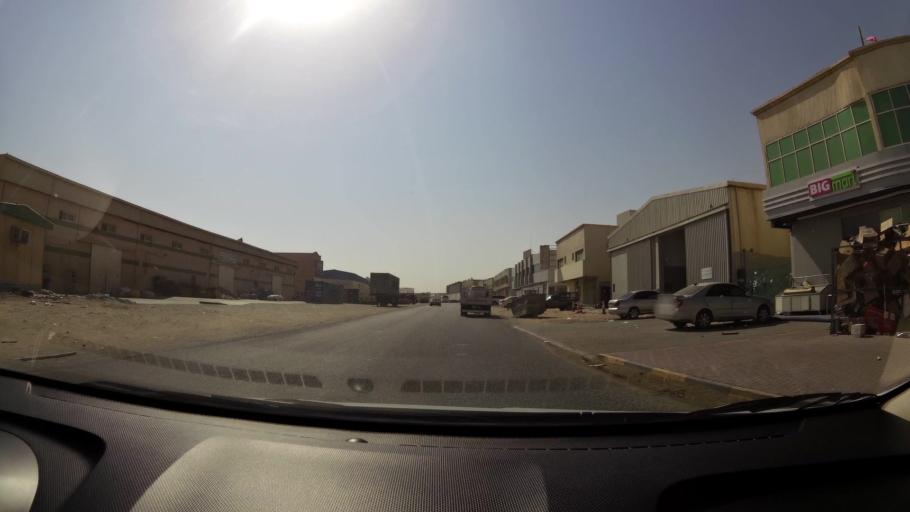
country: AE
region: Ajman
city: Ajman
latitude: 25.4329
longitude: 55.5429
